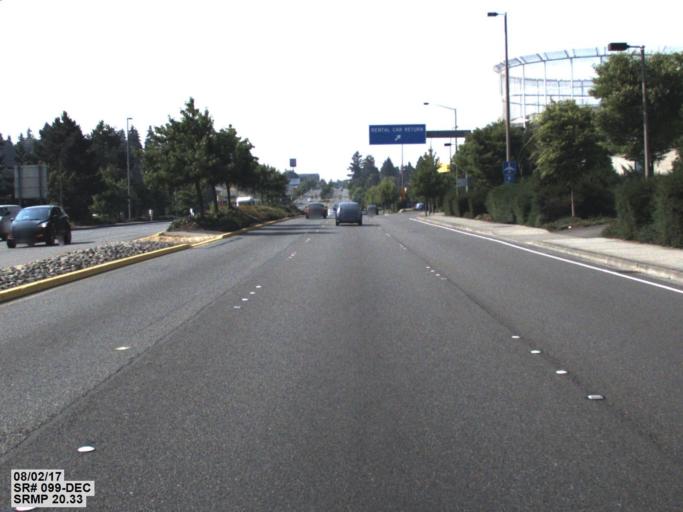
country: US
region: Washington
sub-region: King County
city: SeaTac
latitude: 47.4624
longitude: -122.2904
